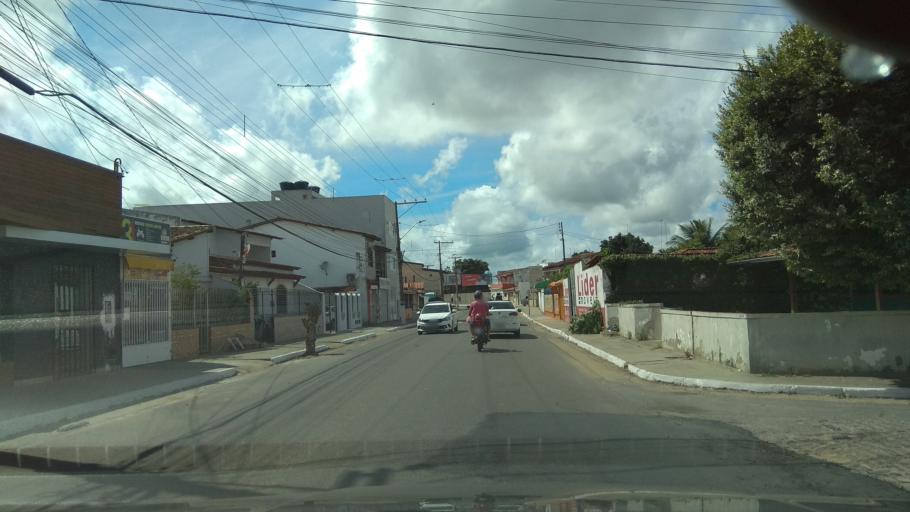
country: BR
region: Bahia
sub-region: Santo Antonio De Jesus
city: Santo Antonio de Jesus
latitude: -12.9732
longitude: -39.2715
